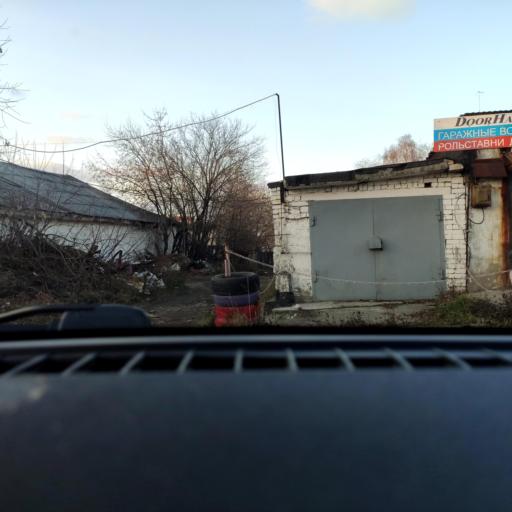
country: RU
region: Perm
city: Perm
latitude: 57.9846
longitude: 56.2374
